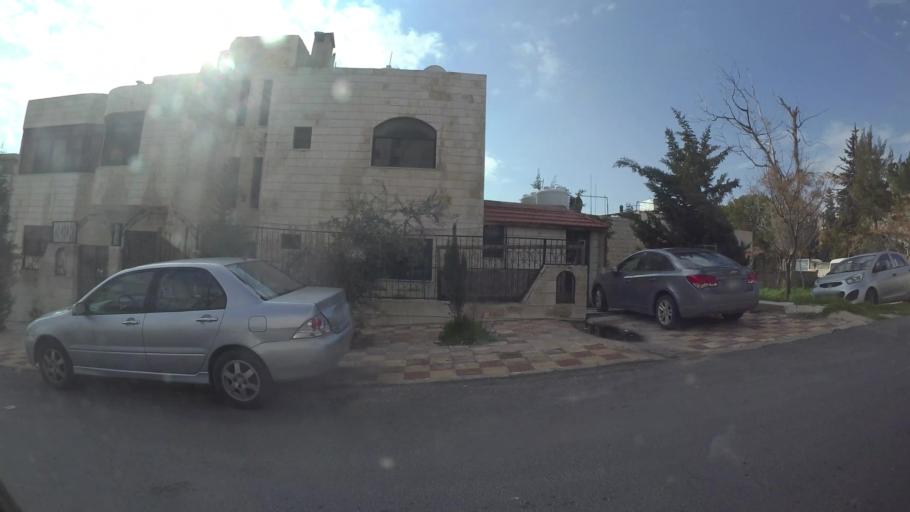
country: JO
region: Amman
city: Al Jubayhah
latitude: 32.0185
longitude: 35.8538
